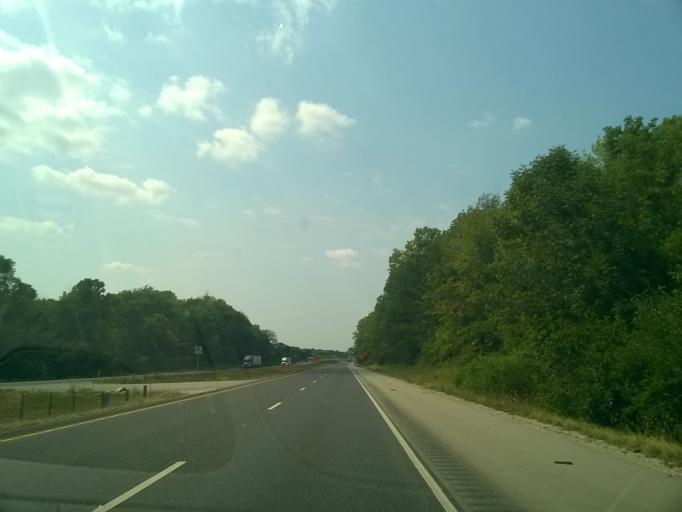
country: US
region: Indiana
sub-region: Vigo County
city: Terre Haute
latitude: 39.4309
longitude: -87.3725
